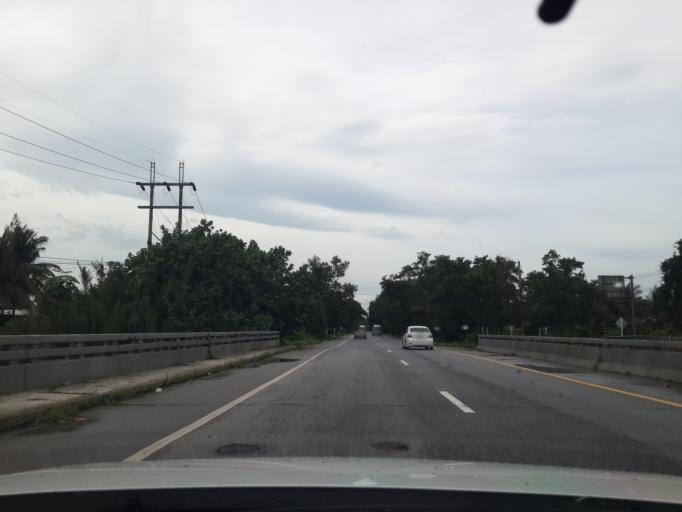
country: TH
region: Songkhla
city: Thepha
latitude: 6.8633
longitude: 100.9588
